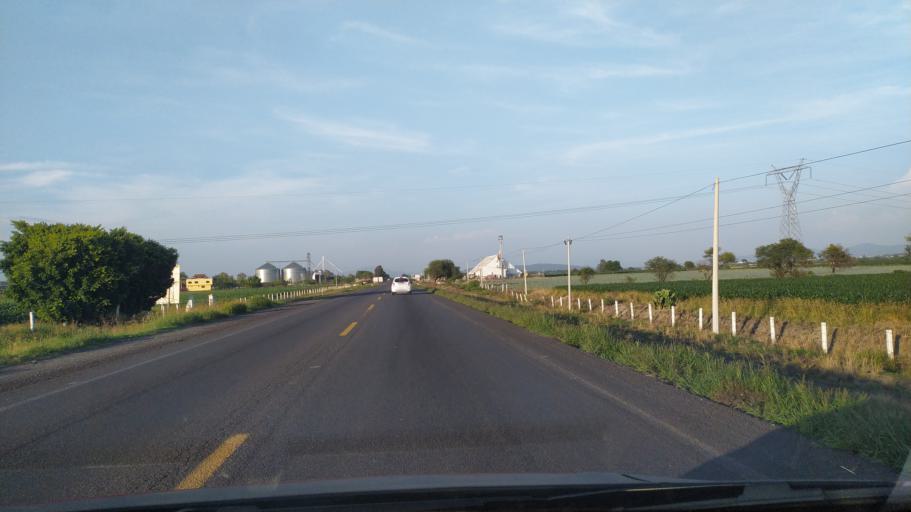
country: MX
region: Michoacan
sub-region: Brisenas
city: Paso de Hidalgo (Paso de Alamos)
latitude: 20.2743
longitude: -102.5193
